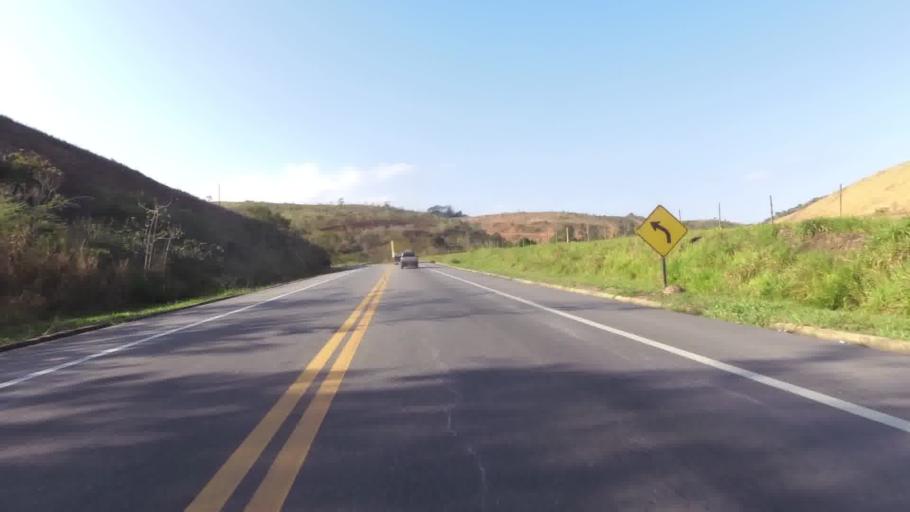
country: BR
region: Espirito Santo
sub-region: Mimoso Do Sul
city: Mimoso do Sul
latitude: -21.1887
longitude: -41.2935
